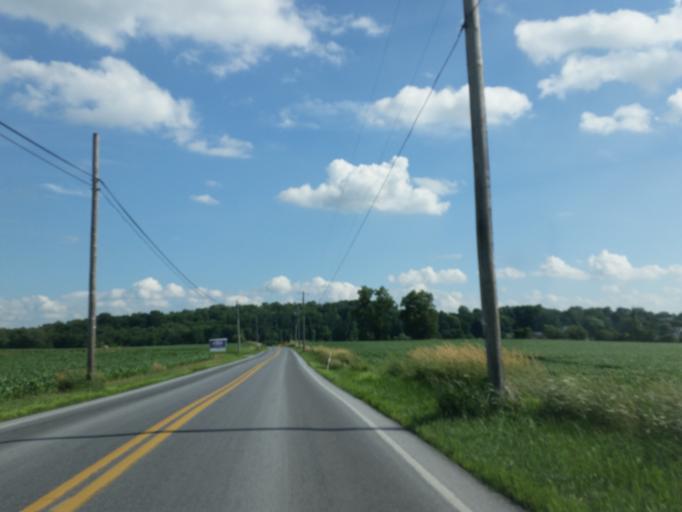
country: US
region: Pennsylvania
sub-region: Lancaster County
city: Strasburg
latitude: 39.9730
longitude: -76.1774
